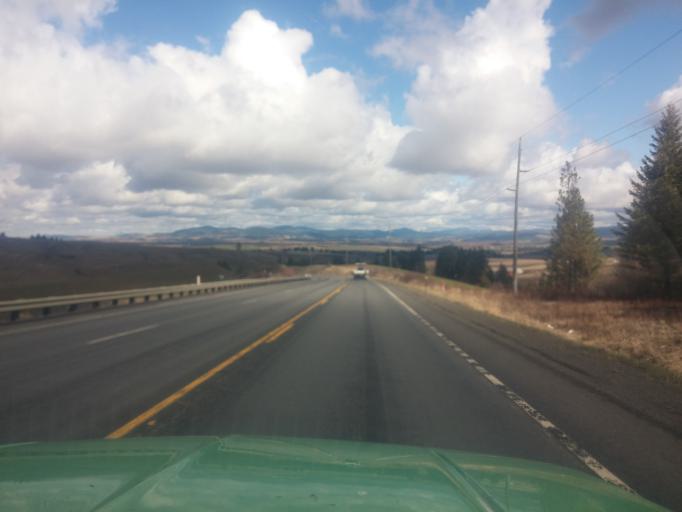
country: US
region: Idaho
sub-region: Latah County
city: Moscow
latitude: 46.8780
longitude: -117.0043
